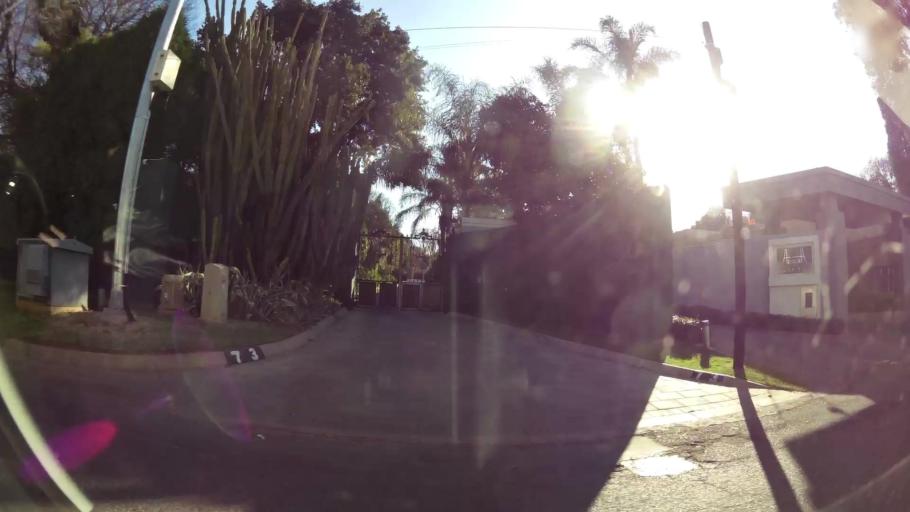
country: ZA
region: Gauteng
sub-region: City of Johannesburg Metropolitan Municipality
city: Johannesburg
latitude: -26.1144
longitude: 28.0655
